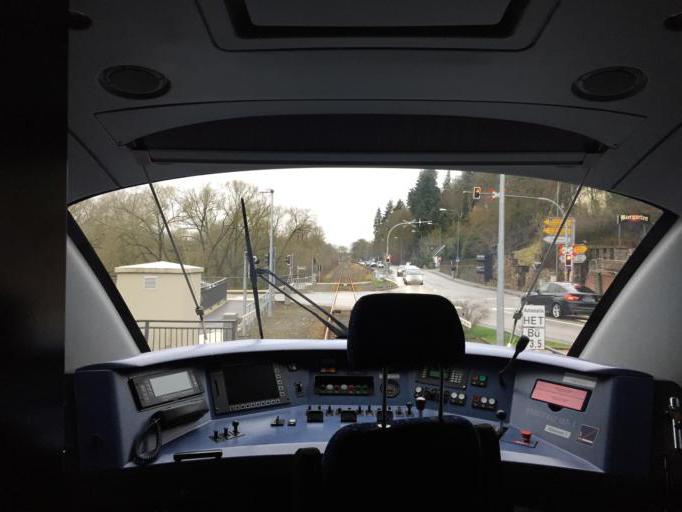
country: DE
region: Hesse
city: Frankenberg
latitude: 51.0651
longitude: 8.7993
